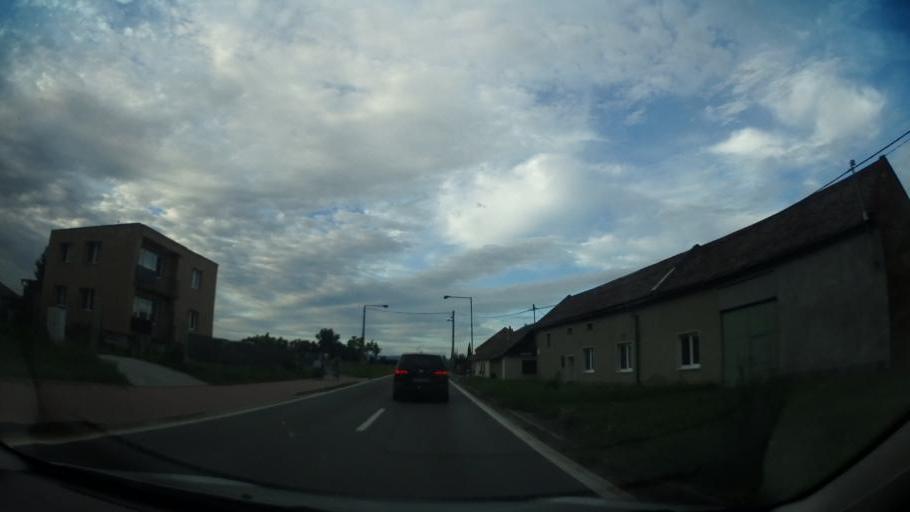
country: CZ
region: Olomoucky
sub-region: Okres Olomouc
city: Unicov
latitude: 49.7512
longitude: 17.0942
